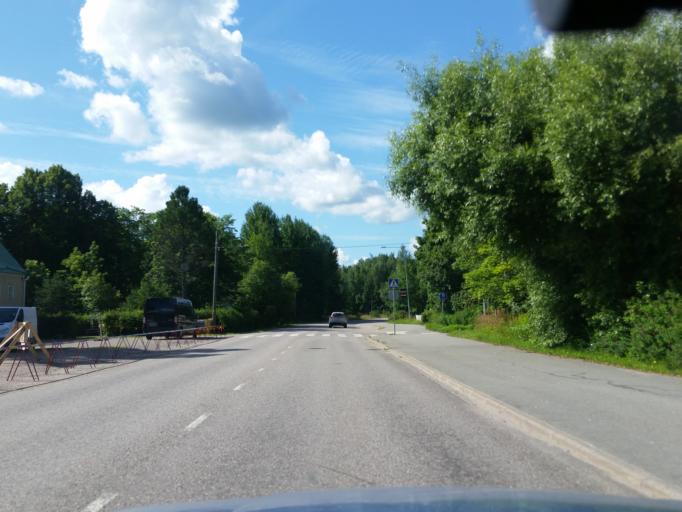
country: FI
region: Uusimaa
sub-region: Helsinki
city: Vihti
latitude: 60.3300
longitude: 24.3168
